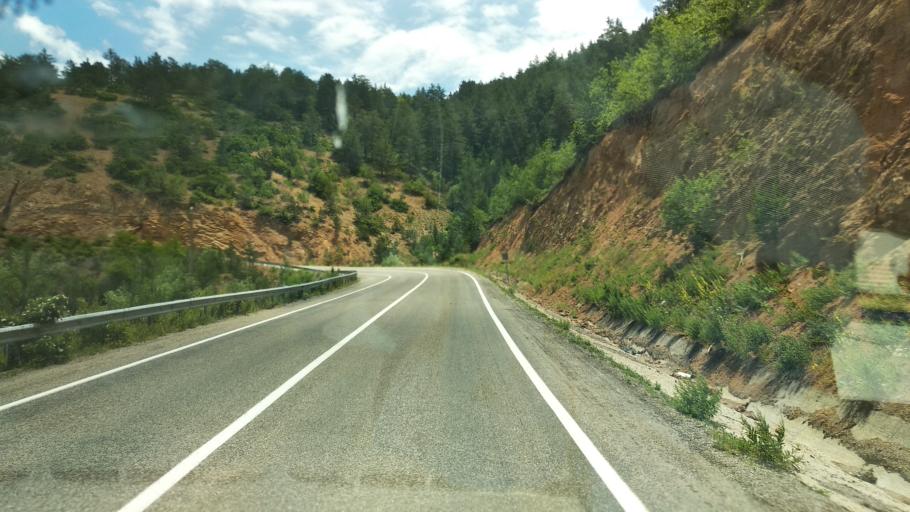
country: TR
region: Gumushane
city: Kose
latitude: 40.2986
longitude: 39.5629
